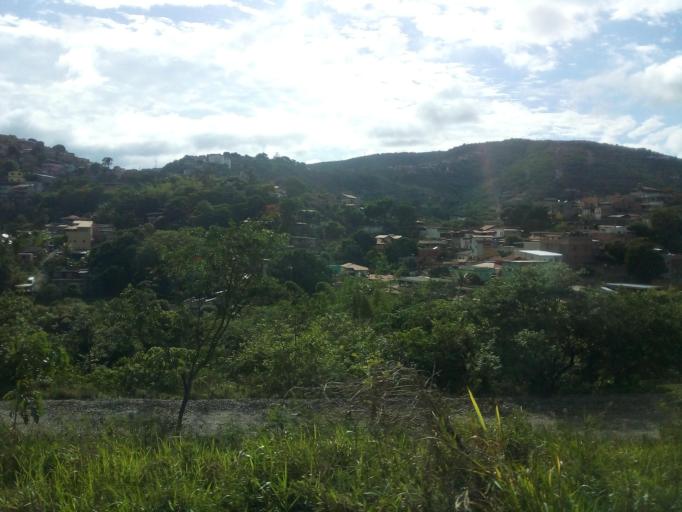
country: BR
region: Minas Gerais
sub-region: Belo Horizonte
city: Belo Horizonte
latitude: -19.8889
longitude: -43.8634
